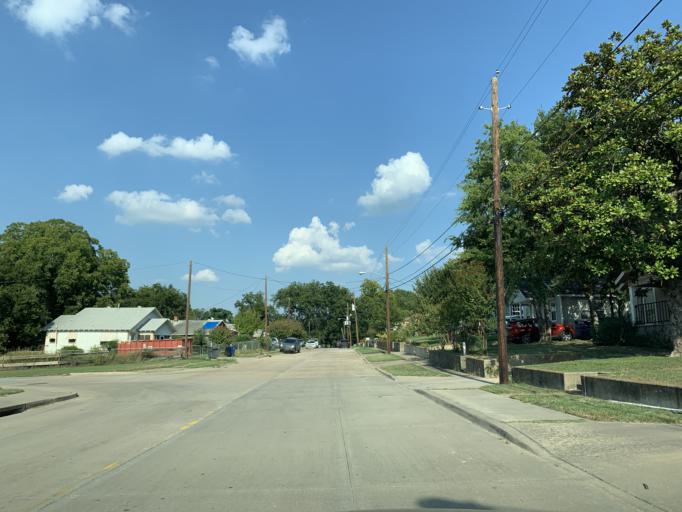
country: US
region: Texas
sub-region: Dallas County
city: Dallas
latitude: 32.7471
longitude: -96.7949
